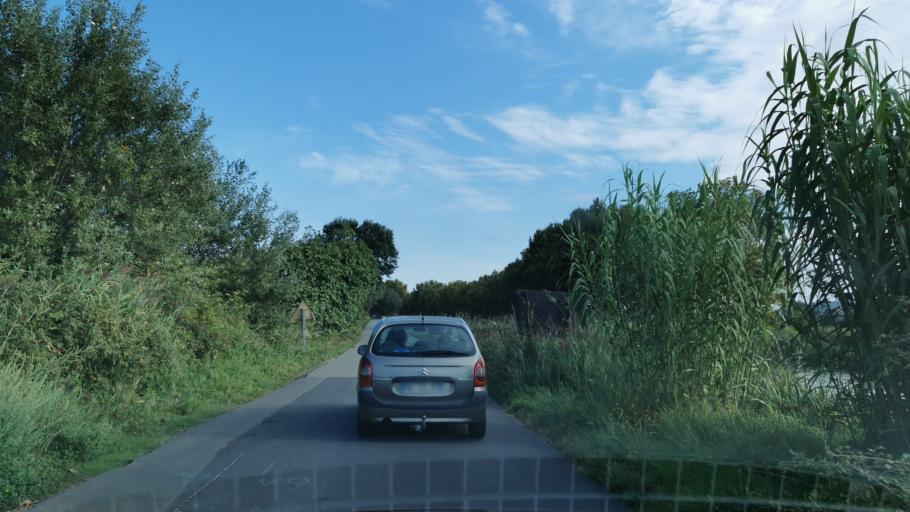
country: FR
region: Languedoc-Roussillon
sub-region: Departement de l'Aude
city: Gruissan
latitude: 43.1228
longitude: 3.0308
